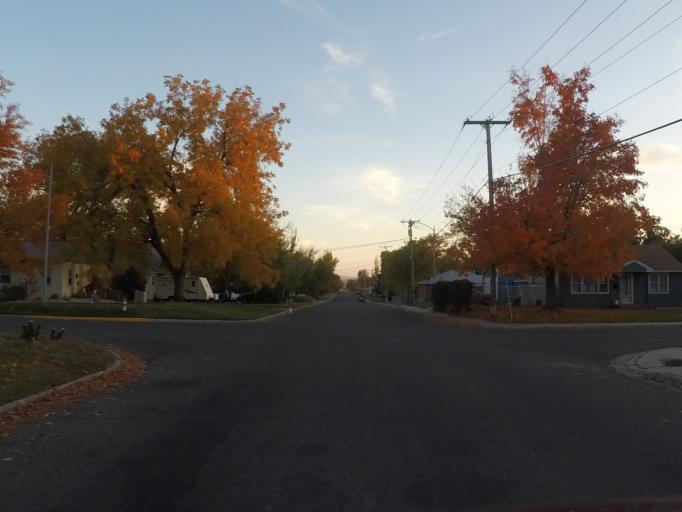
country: US
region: Montana
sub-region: Yellowstone County
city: Billings
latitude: 45.7871
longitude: -108.5410
